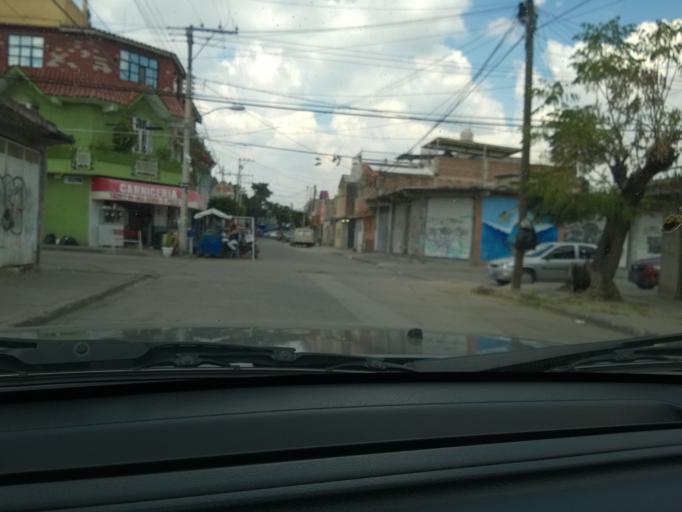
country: MX
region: Guanajuato
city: Leon
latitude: 21.1286
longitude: -101.6518
